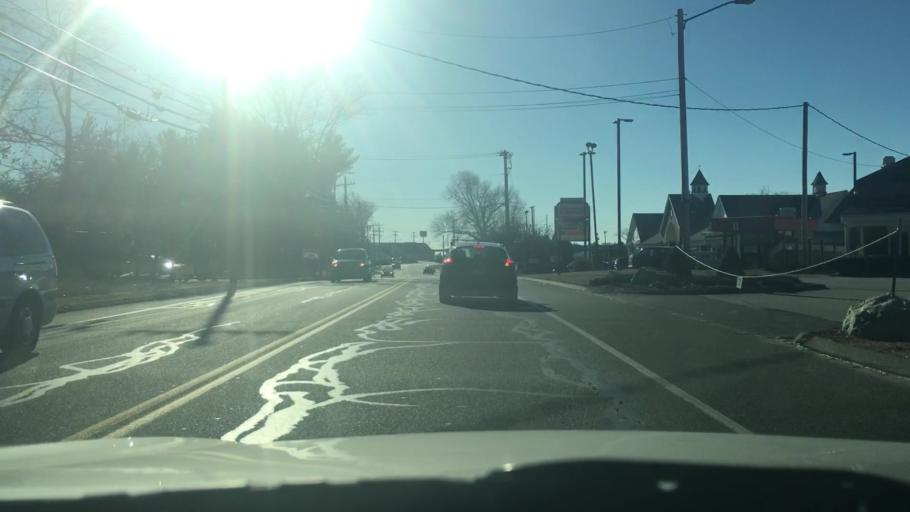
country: US
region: Massachusetts
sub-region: Hampden County
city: North Chicopee
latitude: 42.1695
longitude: -72.5419
